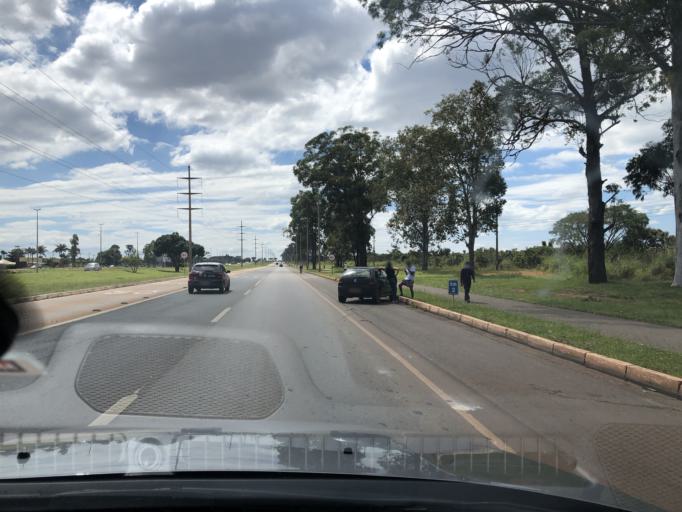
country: BR
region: Federal District
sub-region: Brasilia
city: Brasilia
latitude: -15.9868
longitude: -48.0434
